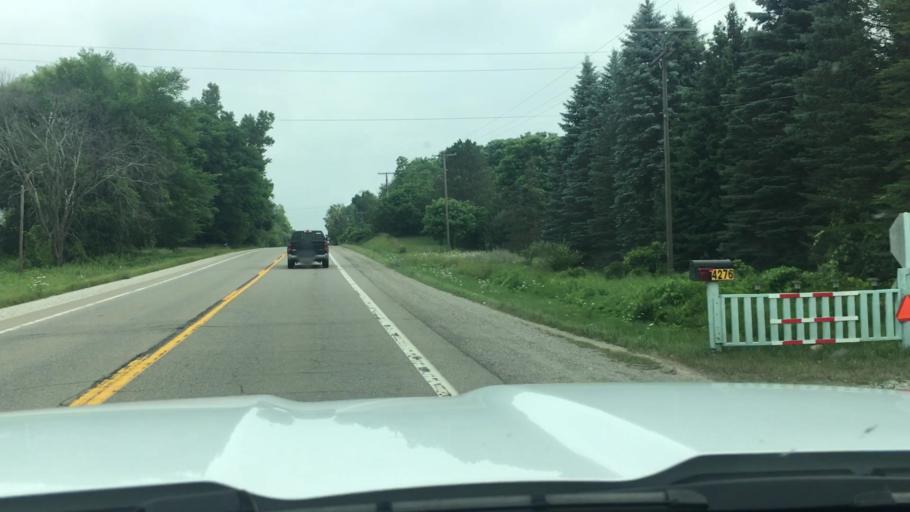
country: US
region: Michigan
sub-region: Sanilac County
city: Brown City
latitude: 43.1611
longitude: -83.0755
